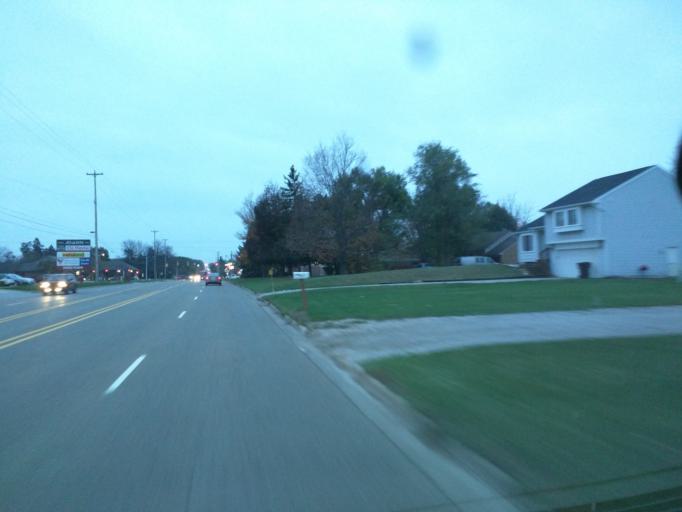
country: US
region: Michigan
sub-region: Ingham County
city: Edgemont Park
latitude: 42.7431
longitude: -84.6030
